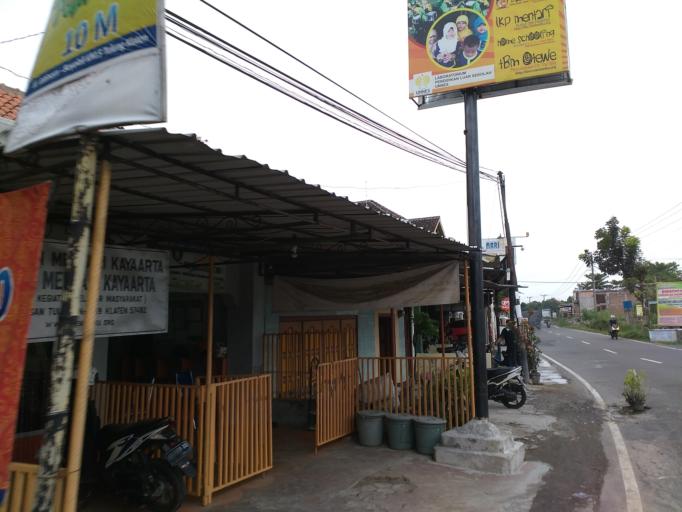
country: ID
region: Central Java
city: Karanganom
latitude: -7.5896
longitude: 110.6219
